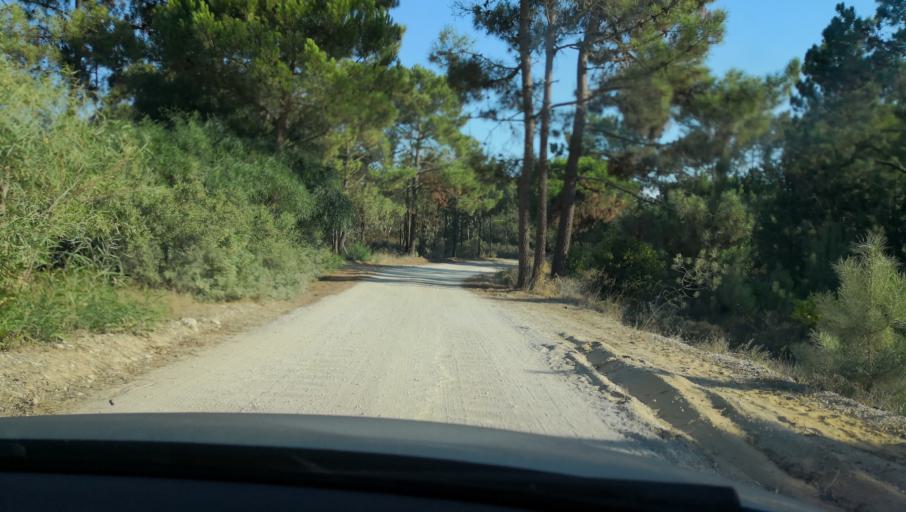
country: PT
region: Setubal
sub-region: Setubal
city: Setubal
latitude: 38.4714
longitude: -8.8779
